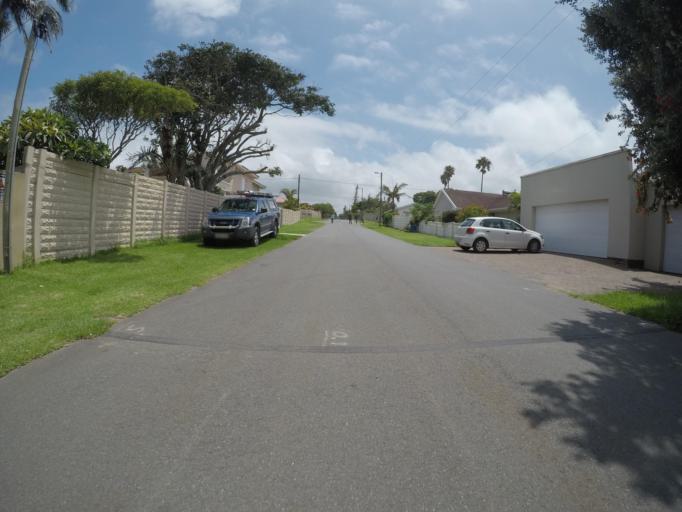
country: ZA
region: Eastern Cape
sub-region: Buffalo City Metropolitan Municipality
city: East London
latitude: -32.9449
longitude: 28.0139
